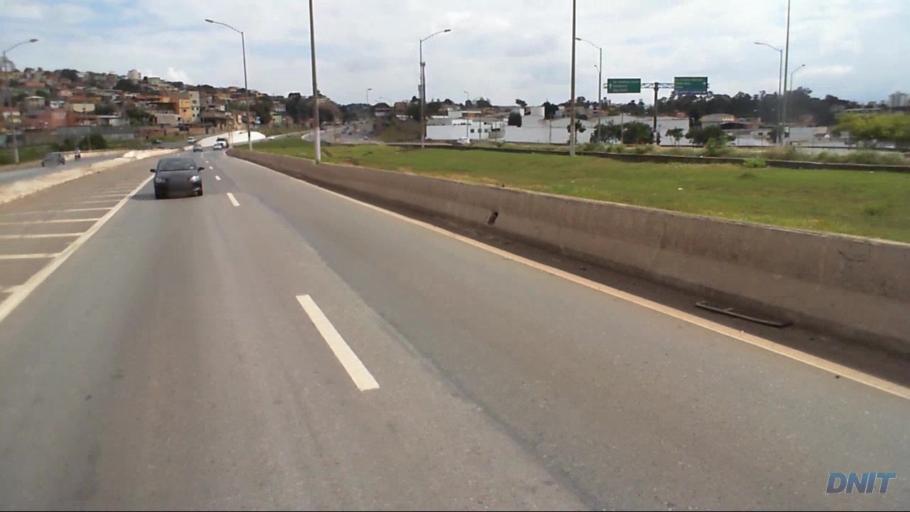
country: BR
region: Minas Gerais
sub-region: Belo Horizonte
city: Belo Horizonte
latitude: -19.8657
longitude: -43.9286
